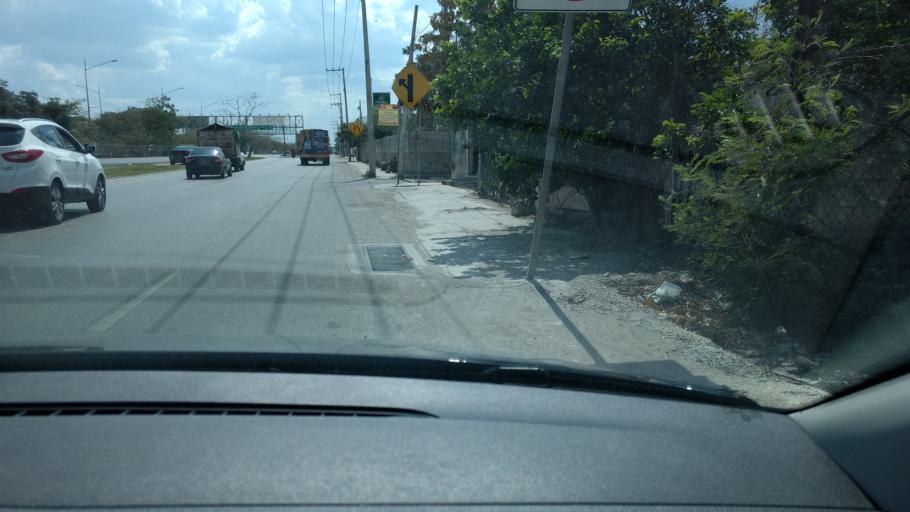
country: MX
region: Yucatan
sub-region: Kanasin
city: Kanasin
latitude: 20.9769
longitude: -89.5649
